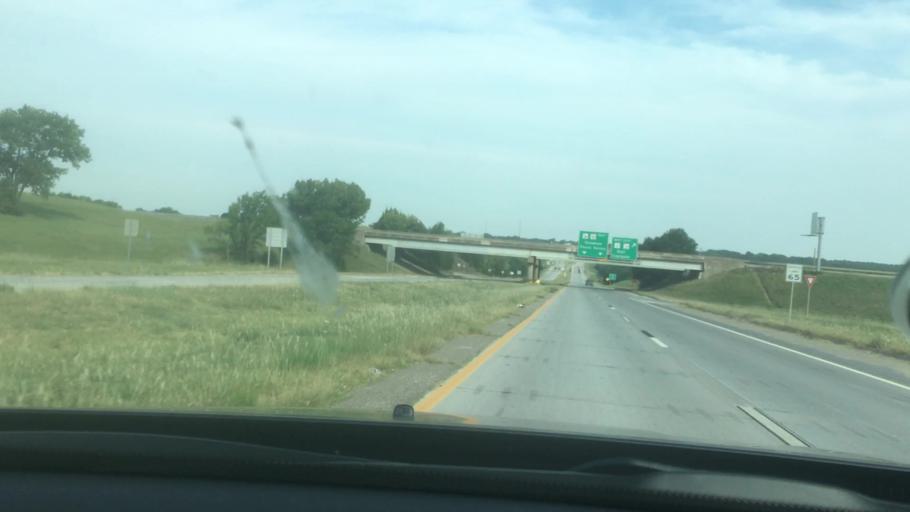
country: US
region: Oklahoma
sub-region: Pontotoc County
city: Ada
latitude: 34.7757
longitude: -96.7006
